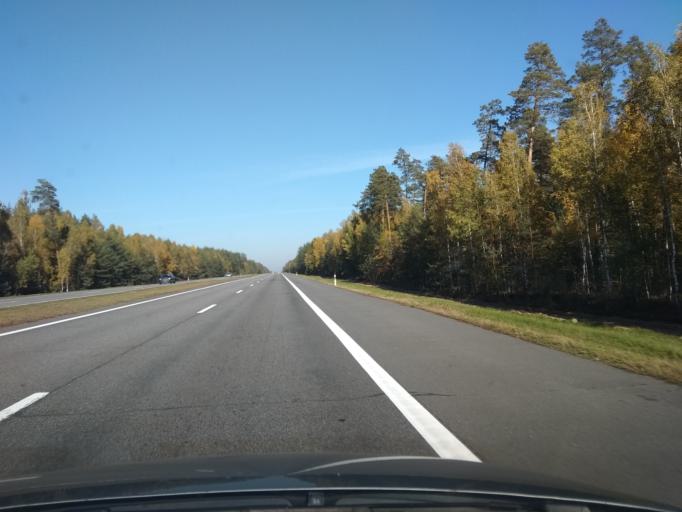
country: BY
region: Grodnenskaya
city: Zhyrovichy
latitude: 52.8792
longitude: 25.6627
